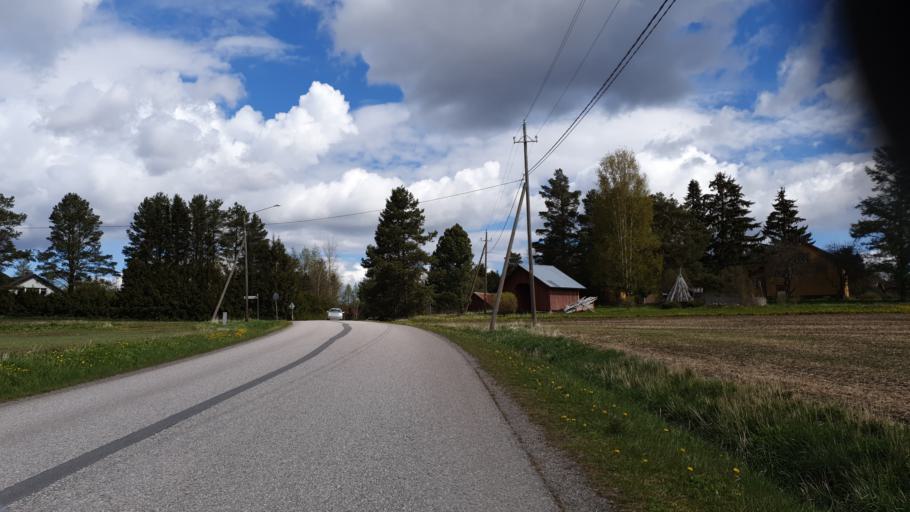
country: FI
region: Uusimaa
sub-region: Helsinki
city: Tuusula
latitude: 60.3985
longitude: 24.9235
